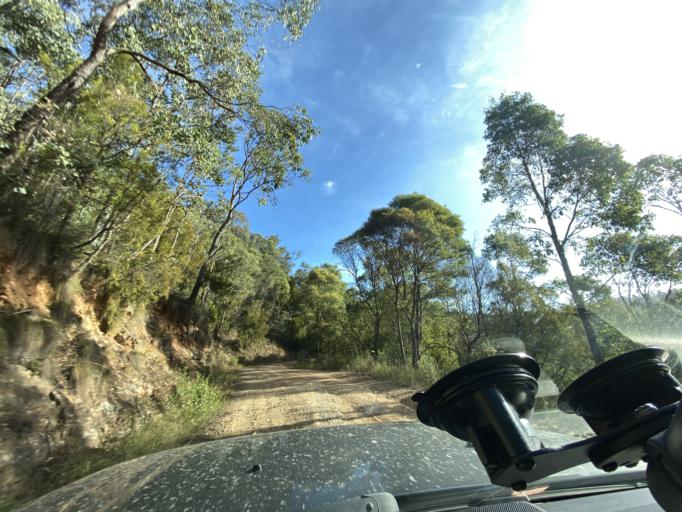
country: AU
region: Victoria
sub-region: Mansfield
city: Mansfield
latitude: -37.5196
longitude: 146.0812
